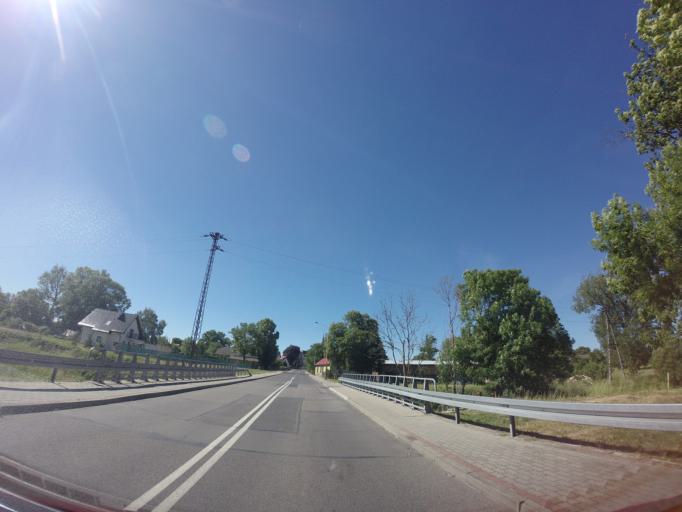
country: PL
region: West Pomeranian Voivodeship
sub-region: Powiat stargardzki
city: Dolice
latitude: 53.1927
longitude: 15.2035
